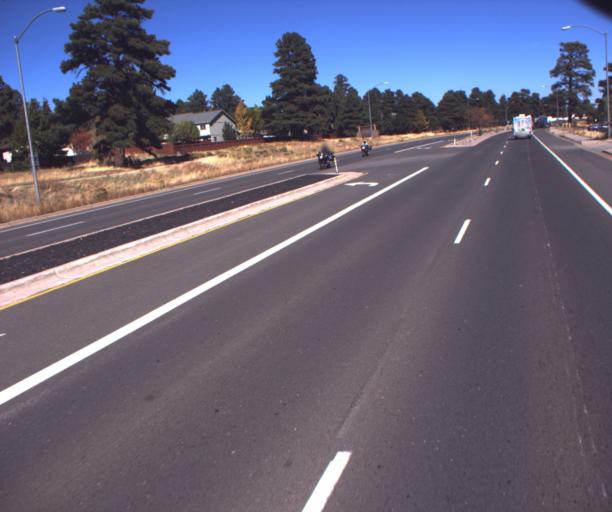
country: US
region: Arizona
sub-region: Coconino County
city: Flagstaff
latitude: 35.2366
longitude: -111.5736
